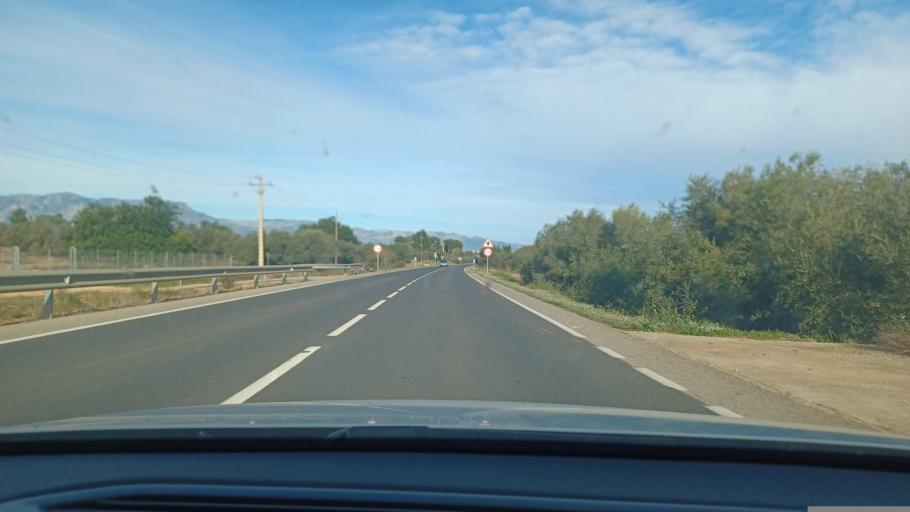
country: ES
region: Catalonia
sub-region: Provincia de Tarragona
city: Santa Barbara
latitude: 40.6884
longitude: 0.5075
